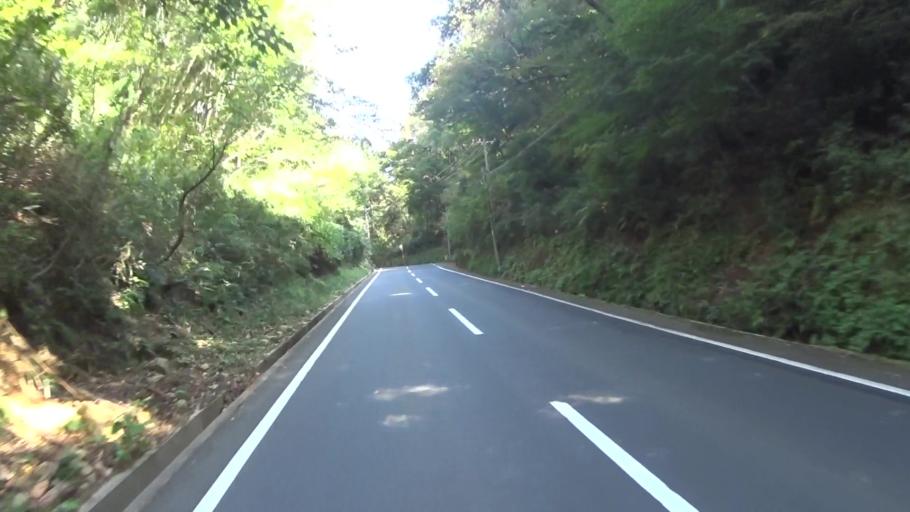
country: JP
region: Kyoto
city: Miyazu
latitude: 35.7468
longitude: 135.2442
